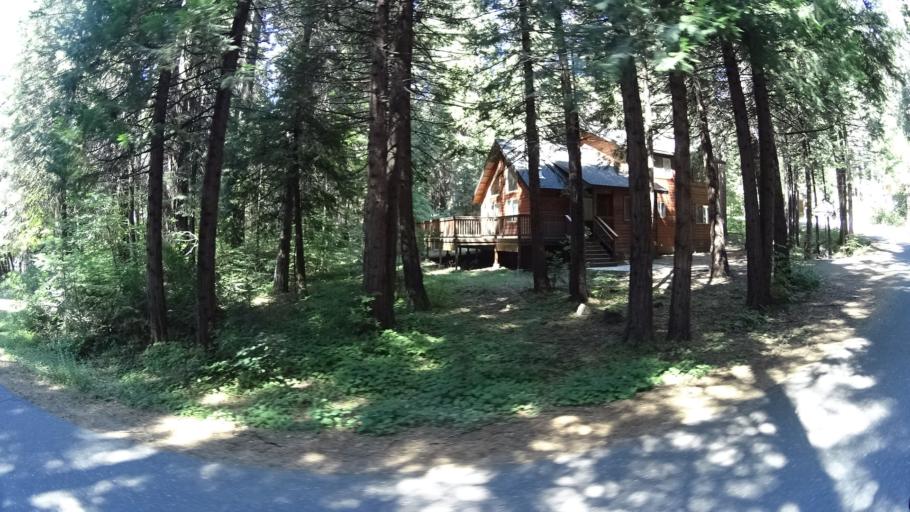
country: US
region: California
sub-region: Calaveras County
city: Arnold
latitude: 38.2942
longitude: -120.2762
